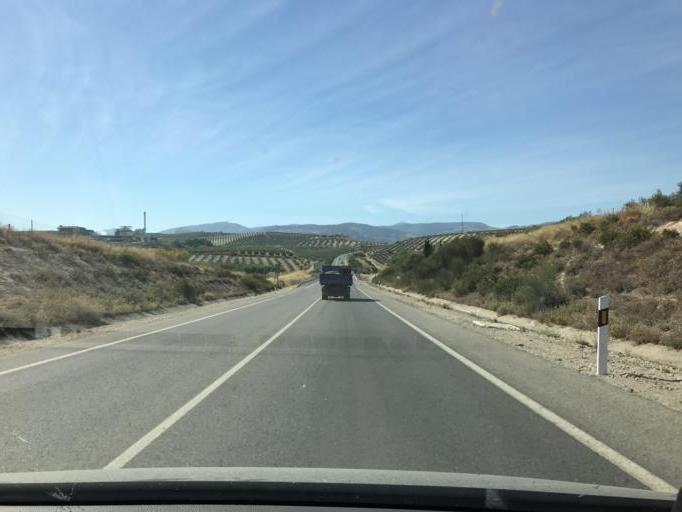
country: ES
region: Andalusia
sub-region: Province of Cordoba
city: Baena
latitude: 37.6177
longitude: -4.3008
